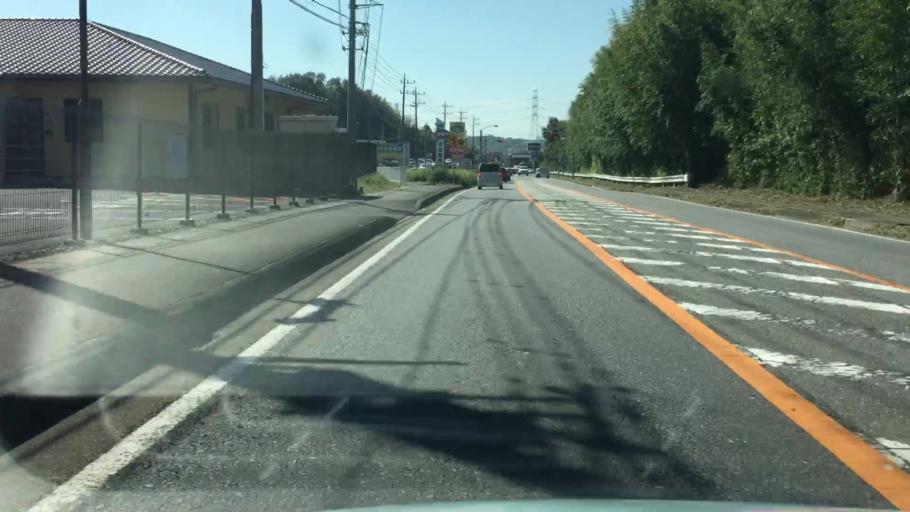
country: JP
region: Ibaraki
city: Ryugasaki
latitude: 35.8771
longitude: 140.1567
